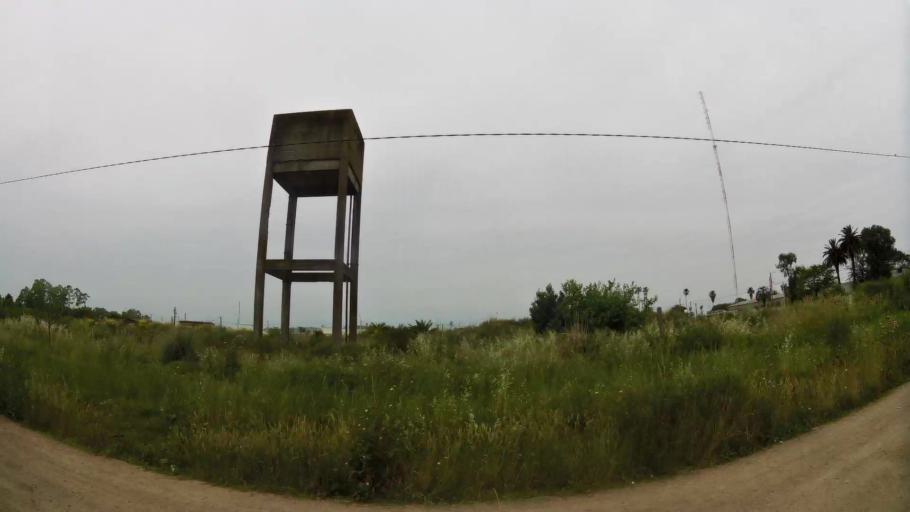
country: UY
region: Canelones
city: La Paz
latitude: -34.7464
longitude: -56.2231
